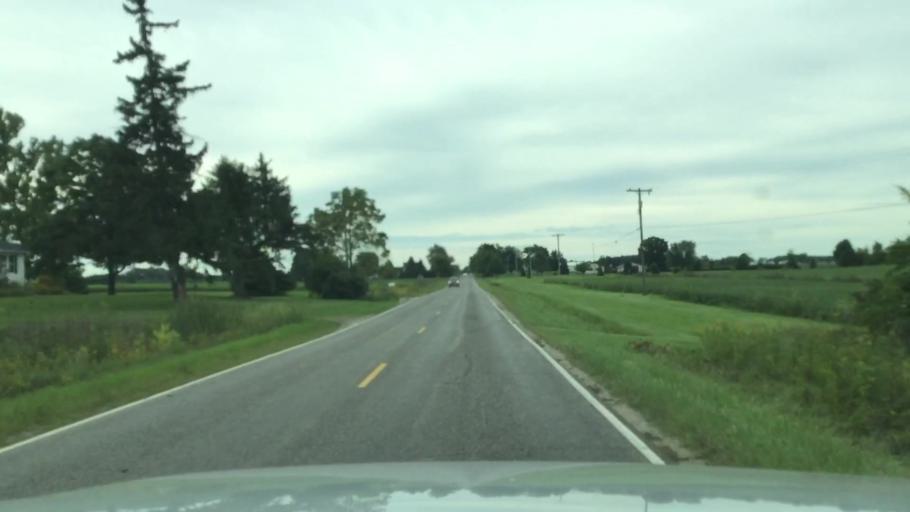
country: US
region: Michigan
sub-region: Genesee County
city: Flushing
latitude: 43.0553
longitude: -83.9875
